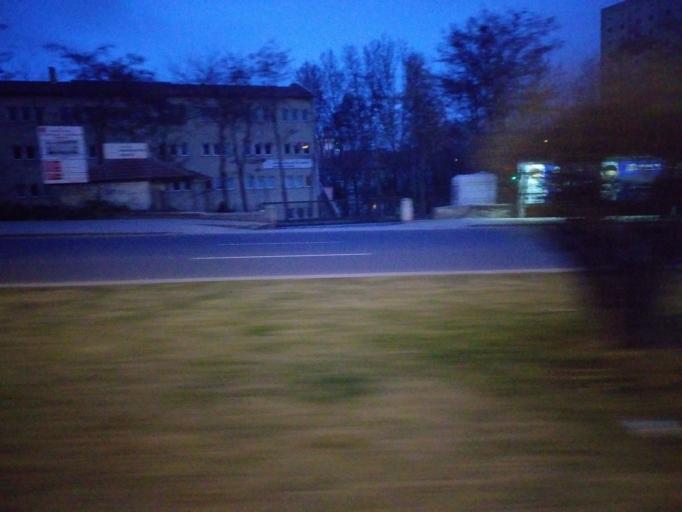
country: TR
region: Ankara
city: Ankara
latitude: 39.9676
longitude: 32.8382
